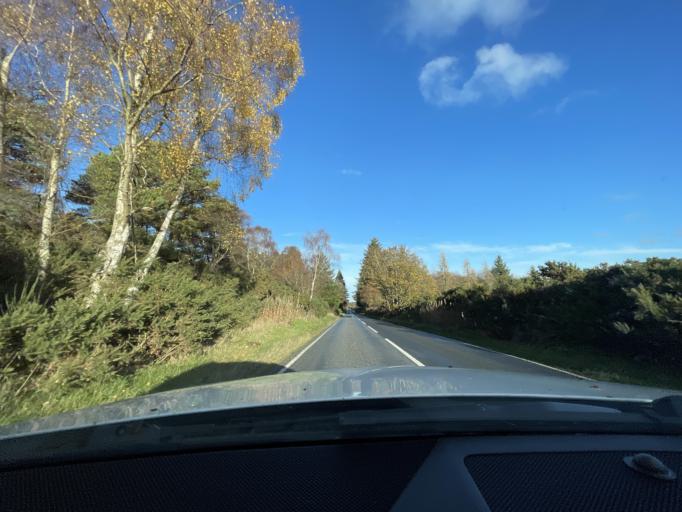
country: GB
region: Scotland
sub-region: Highland
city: Inverness
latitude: 57.4143
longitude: -4.3047
